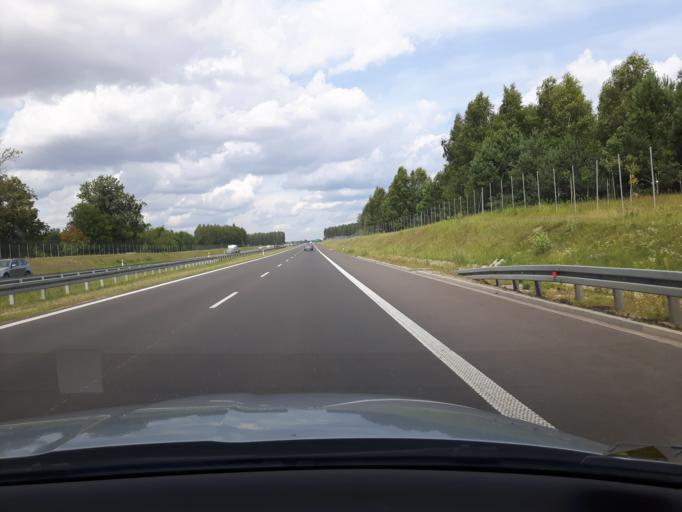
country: PL
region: Masovian Voivodeship
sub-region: Powiat mlawski
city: Wieczfnia Koscielna
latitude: 53.2634
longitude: 20.4290
